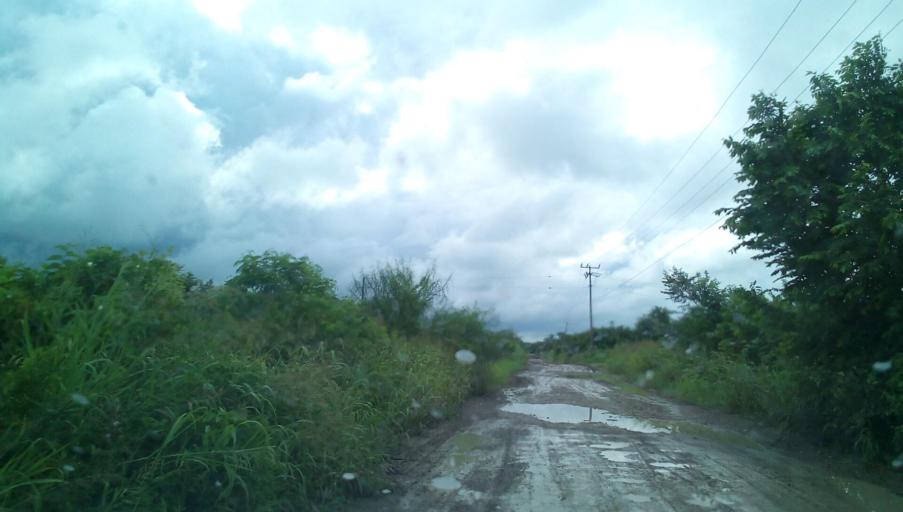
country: MX
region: Veracruz
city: Panuco
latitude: 21.8482
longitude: -98.1404
